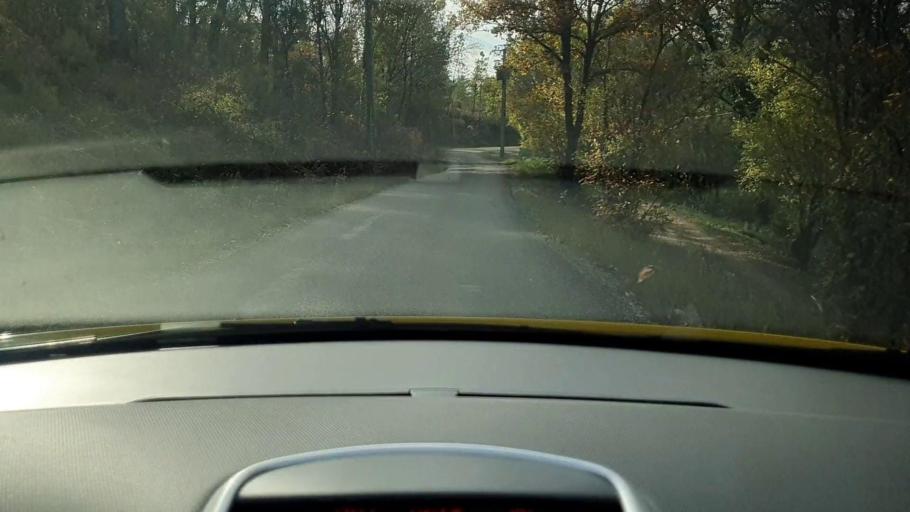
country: FR
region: Languedoc-Roussillon
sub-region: Departement du Gard
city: Lasalle
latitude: 44.0360
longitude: 3.8986
